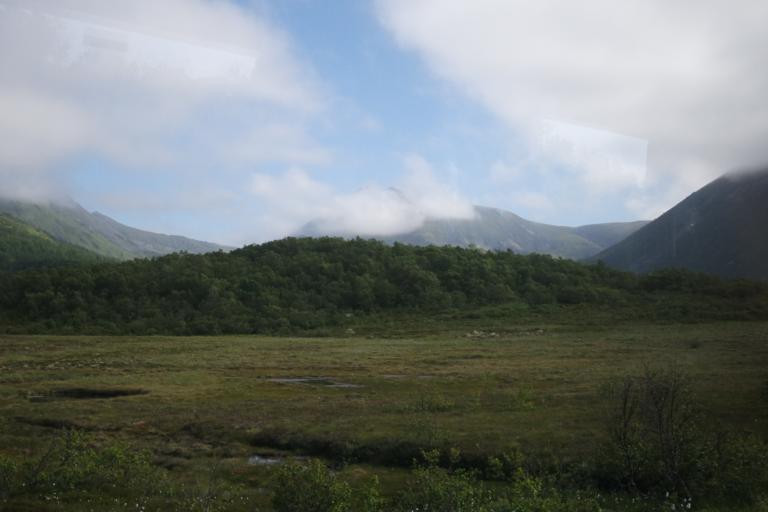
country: NO
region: Nordland
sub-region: Sortland
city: Sortland
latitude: 69.0092
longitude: 15.5543
